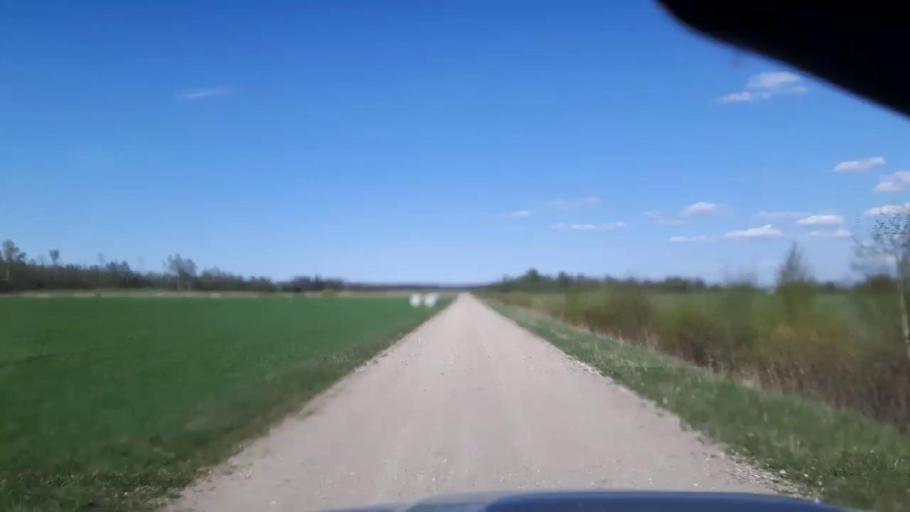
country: EE
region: Paernumaa
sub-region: Tootsi vald
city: Tootsi
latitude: 58.5310
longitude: 24.8269
